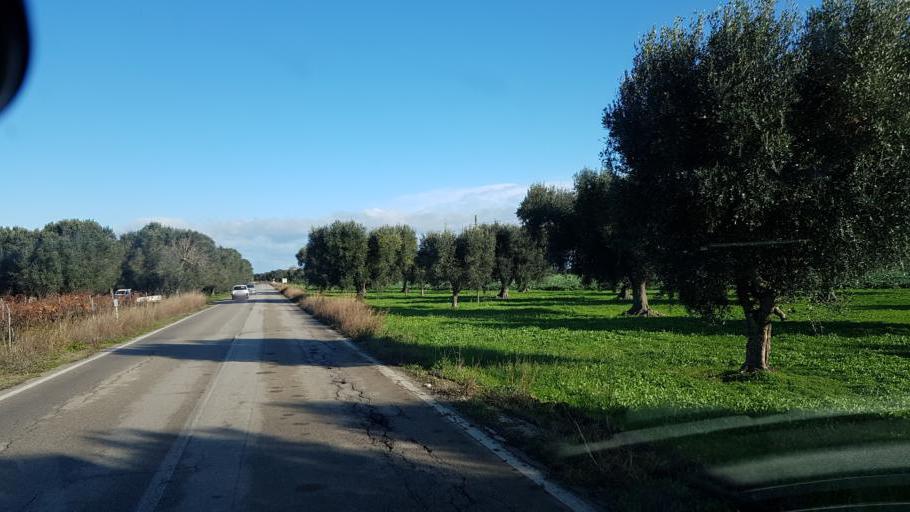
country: IT
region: Apulia
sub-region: Provincia di Brindisi
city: Tuturano
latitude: 40.5595
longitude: 17.9479
